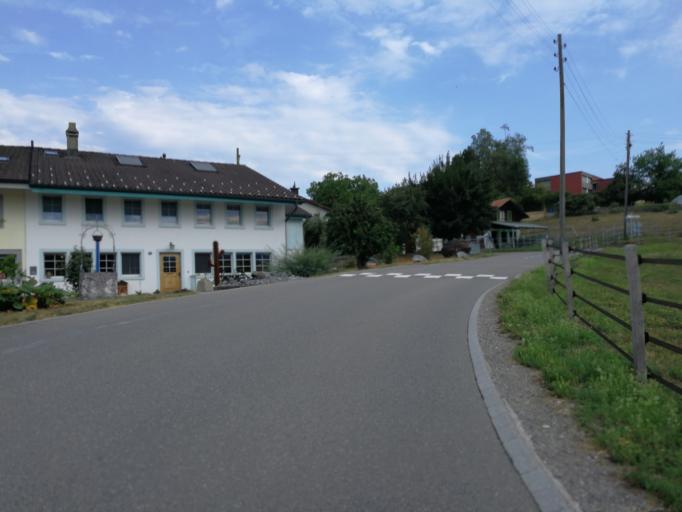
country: CH
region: Zurich
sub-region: Bezirk Hinwil
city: Gossau
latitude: 47.3292
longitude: 8.7601
